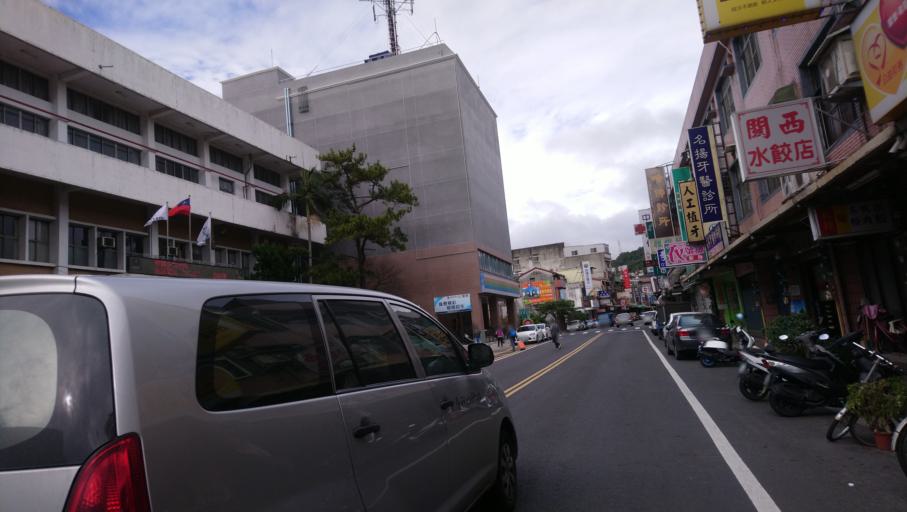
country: TW
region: Taiwan
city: Daxi
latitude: 24.7923
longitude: 121.1761
